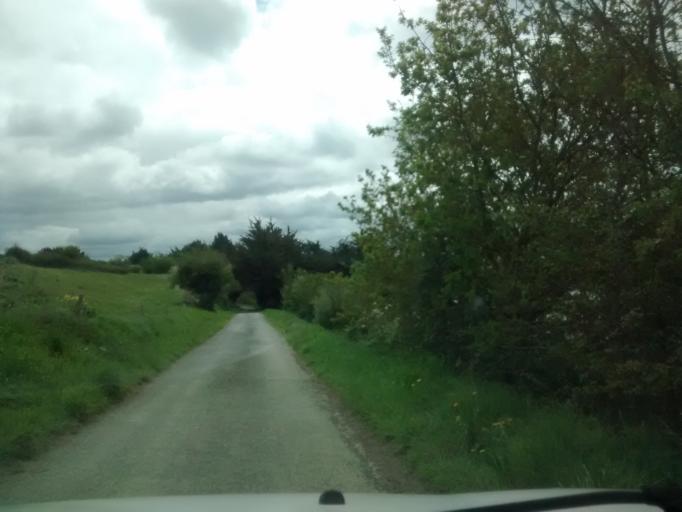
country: FR
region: Brittany
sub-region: Departement d'Ille-et-Vilaine
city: Saint-Jouan-des-Guerets
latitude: 48.5833
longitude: -1.9629
